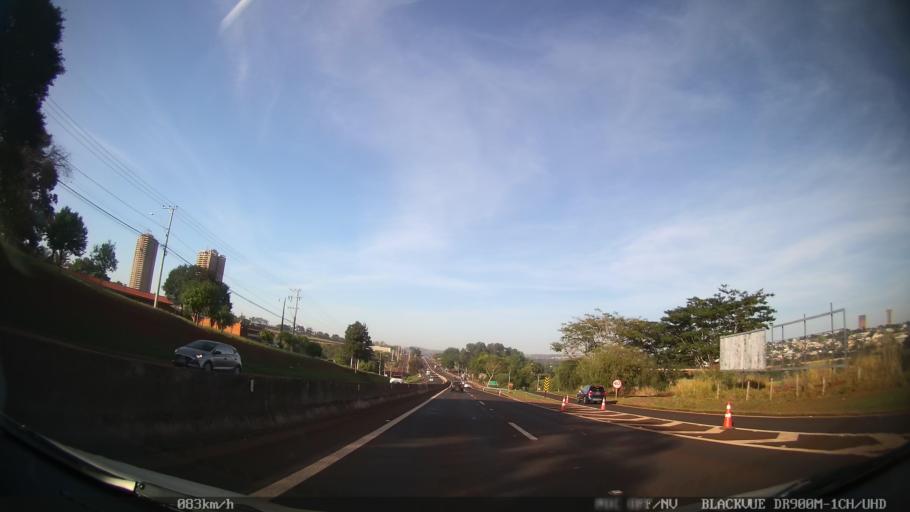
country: BR
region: Sao Paulo
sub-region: Ribeirao Preto
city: Ribeirao Preto
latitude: -21.2336
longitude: -47.8185
